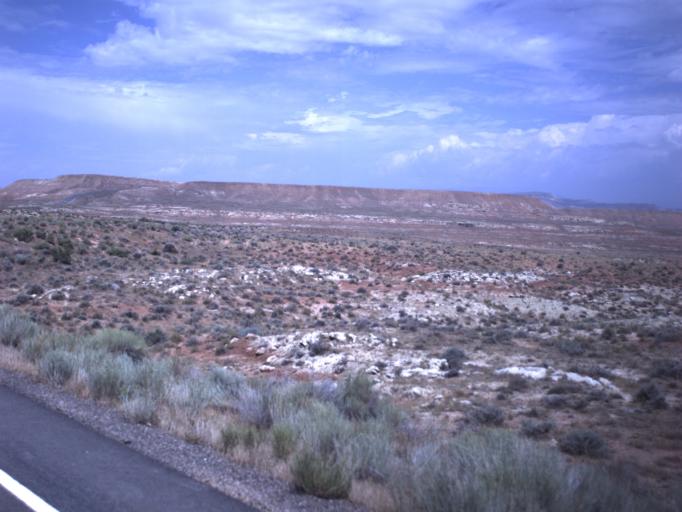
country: US
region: Utah
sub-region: Uintah County
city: Naples
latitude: 40.2620
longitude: -109.4413
